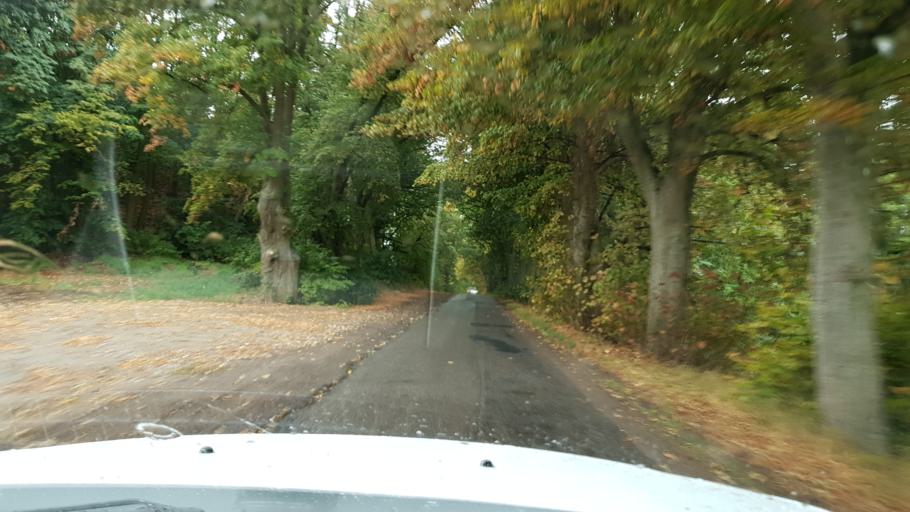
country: DE
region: Brandenburg
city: Schwedt (Oder)
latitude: 53.0056
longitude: 14.2925
